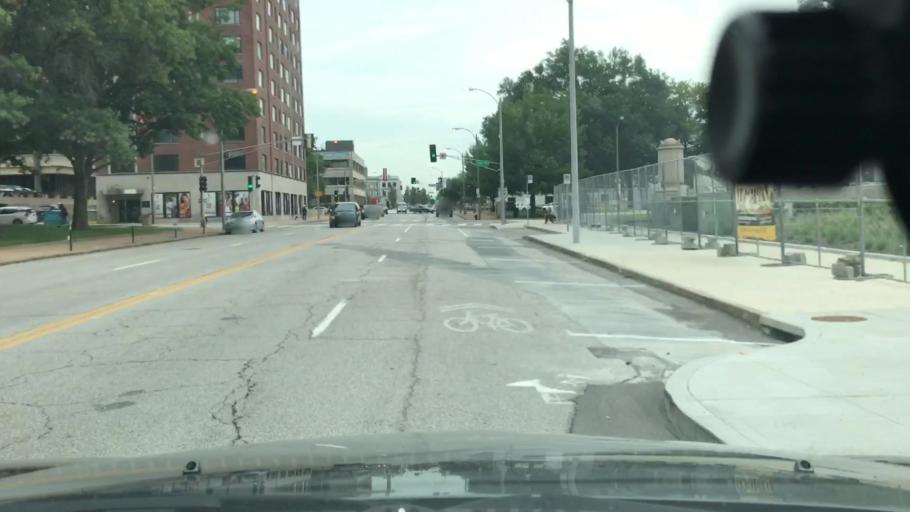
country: US
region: Missouri
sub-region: City of Saint Louis
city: St. Louis
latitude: 38.6289
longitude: -90.2007
